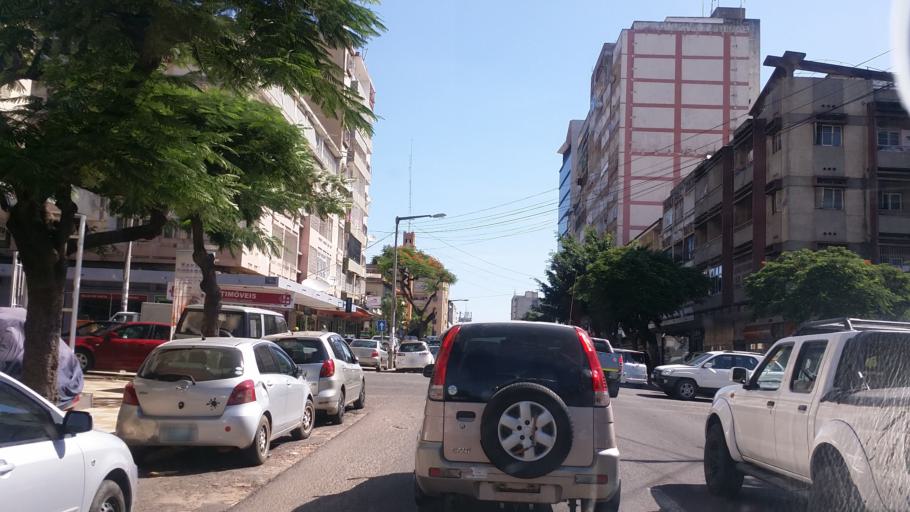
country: MZ
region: Maputo City
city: Maputo
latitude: -25.9643
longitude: 32.5805
